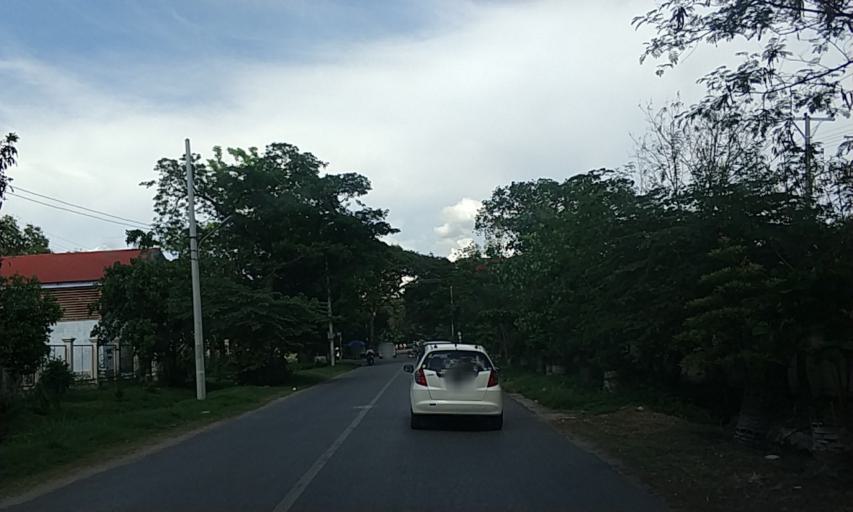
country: MM
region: Mandalay
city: Mandalay
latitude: 21.9789
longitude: 96.1057
